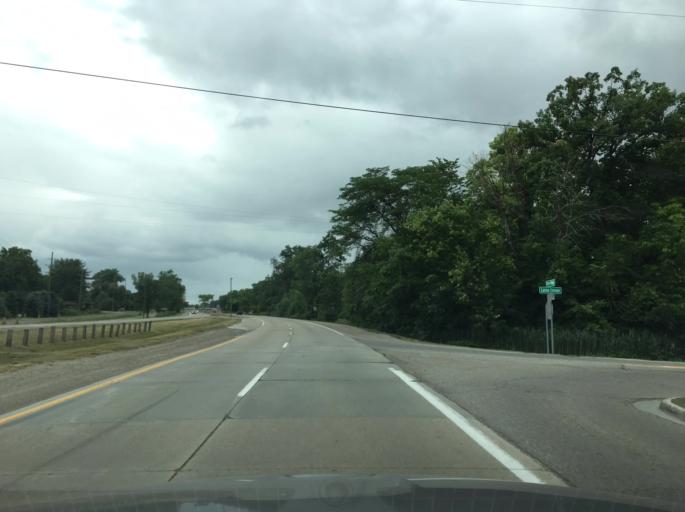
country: US
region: Michigan
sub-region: Macomb County
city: Mount Clemens
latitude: 42.5739
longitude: -82.8450
